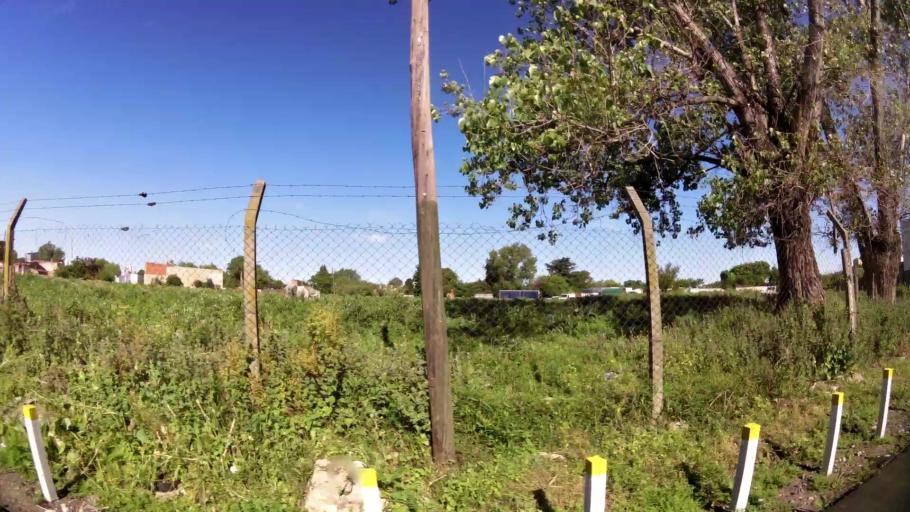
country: AR
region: Buenos Aires
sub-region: Partido de Lomas de Zamora
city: Lomas de Zamora
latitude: -34.7714
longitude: -58.4200
